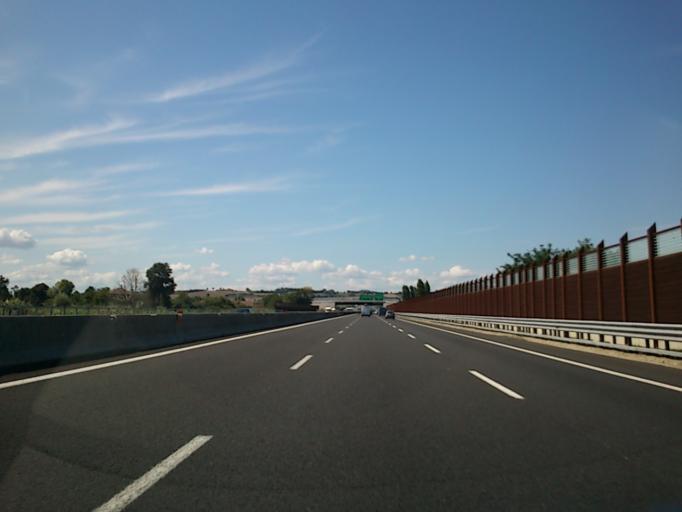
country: IT
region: The Marches
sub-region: Provincia di Pesaro e Urbino
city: Pesaro
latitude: 43.8995
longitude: 12.8591
